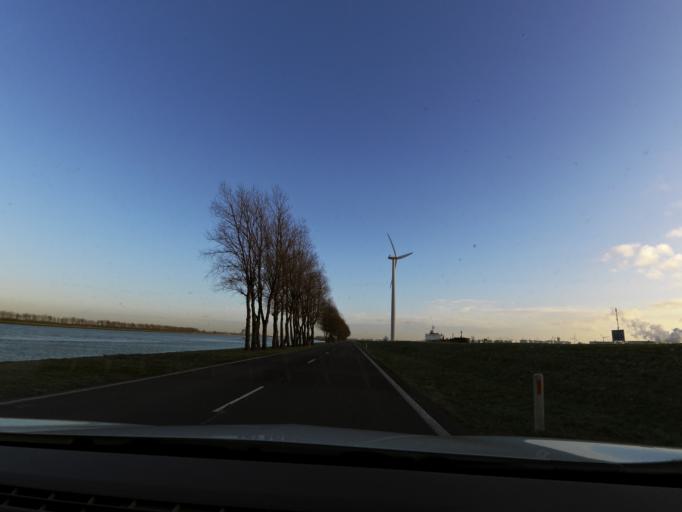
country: NL
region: South Holland
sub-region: Gemeente Westland
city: Maasdijk
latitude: 51.9451
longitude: 4.1749
